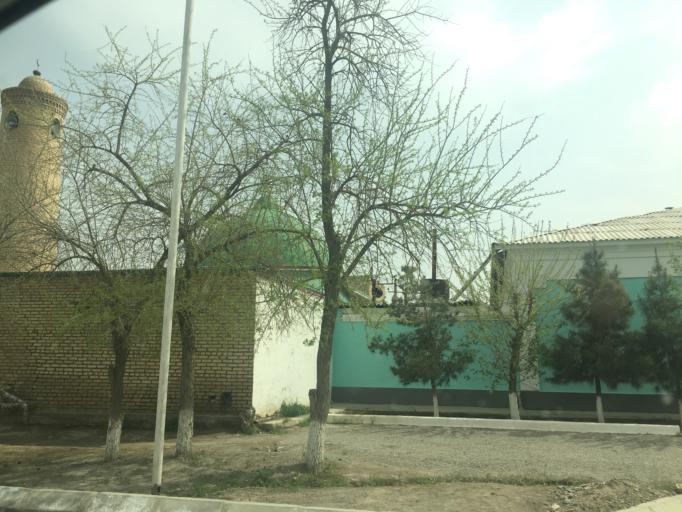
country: TM
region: Mary
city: Mary
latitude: 37.5976
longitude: 61.8658
